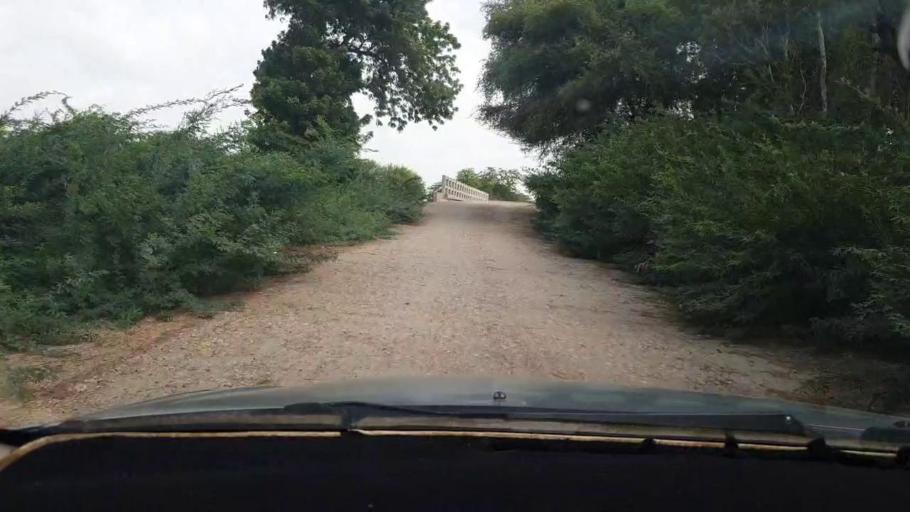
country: PK
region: Sindh
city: Tando Bago
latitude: 24.7683
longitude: 69.0230
